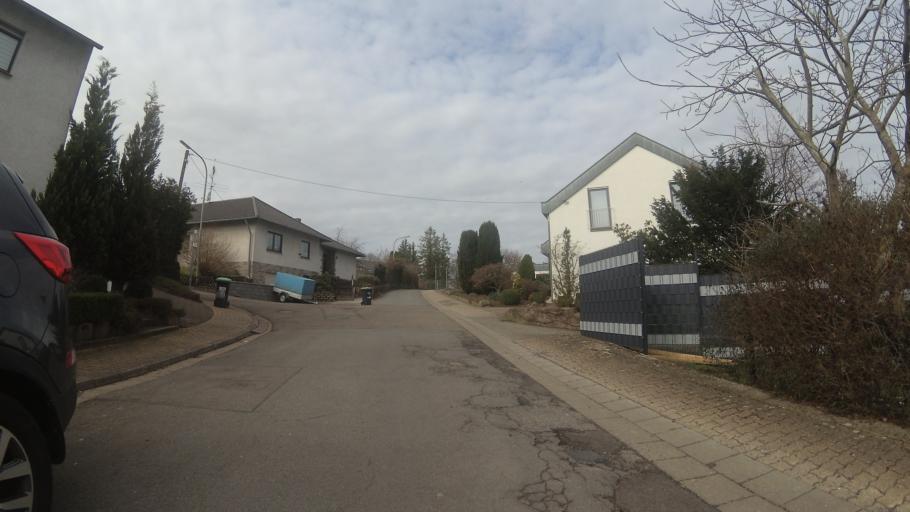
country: FR
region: Lorraine
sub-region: Departement de la Moselle
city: Merten
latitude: 49.2951
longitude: 6.6534
